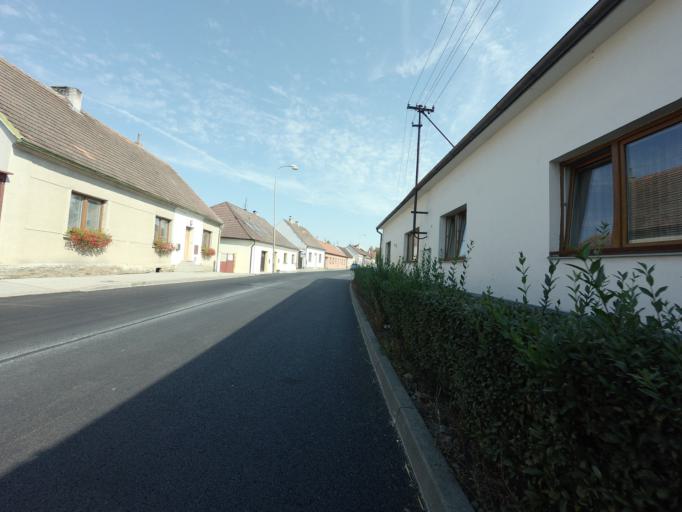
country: CZ
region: Jihocesky
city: Bernartice
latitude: 49.3663
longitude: 14.3787
